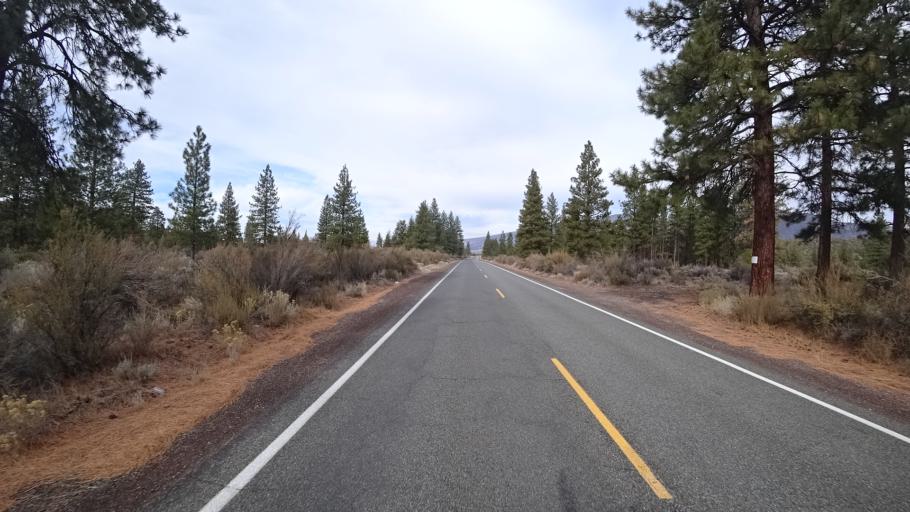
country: US
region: California
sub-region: Siskiyou County
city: Weed
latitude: 41.5441
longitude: -122.2467
